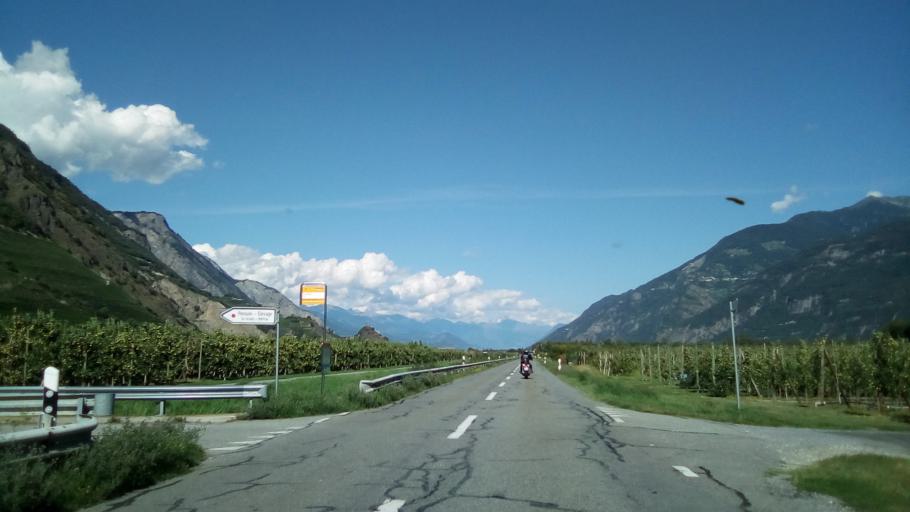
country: CH
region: Valais
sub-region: Martigny District
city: Saxon
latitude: 46.1566
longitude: 7.1562
